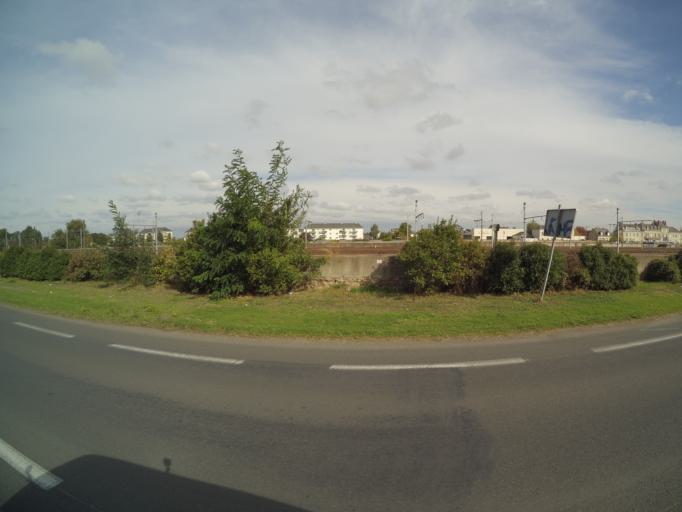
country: FR
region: Pays de la Loire
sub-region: Departement de Maine-et-Loire
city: Saumur
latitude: 47.2706
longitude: -0.0761
